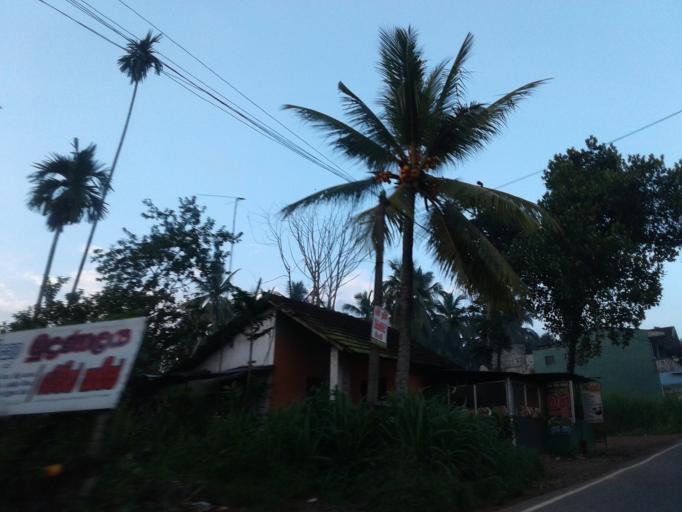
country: LK
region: Western
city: Gampaha
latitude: 7.0284
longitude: 80.0283
